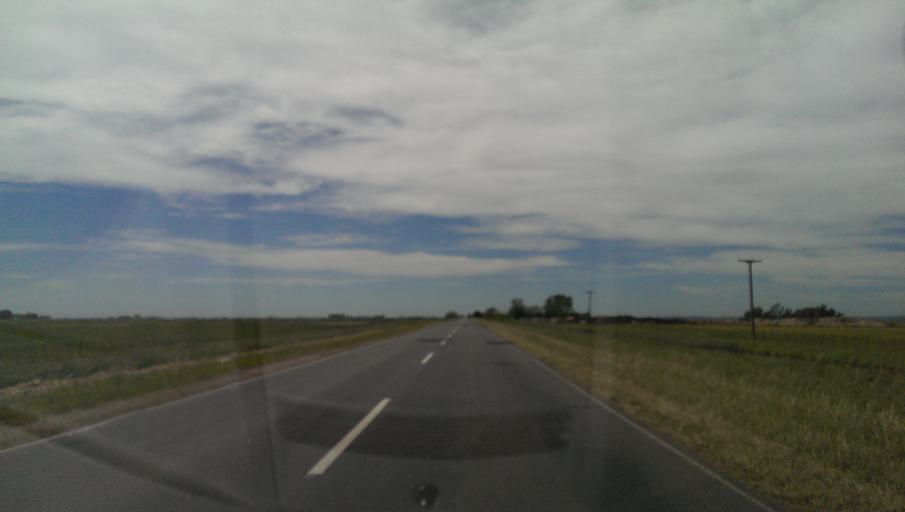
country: AR
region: Buenos Aires
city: Olavarria
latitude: -37.0398
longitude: -60.4348
